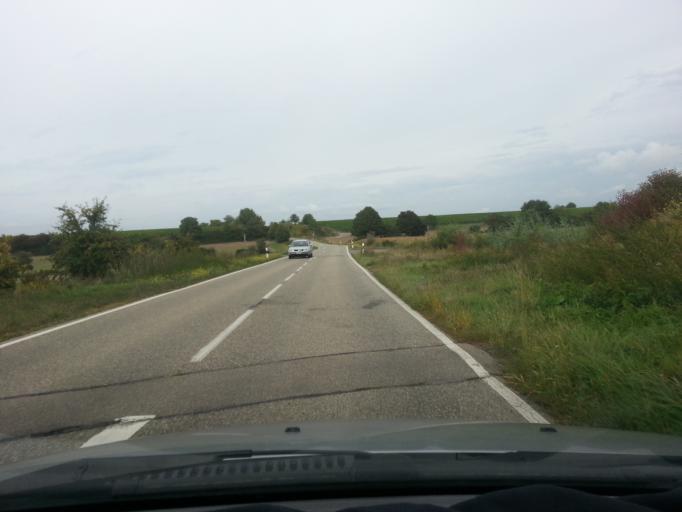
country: DE
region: Rheinland-Pfalz
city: Essingen
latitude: 49.2468
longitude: 8.1729
